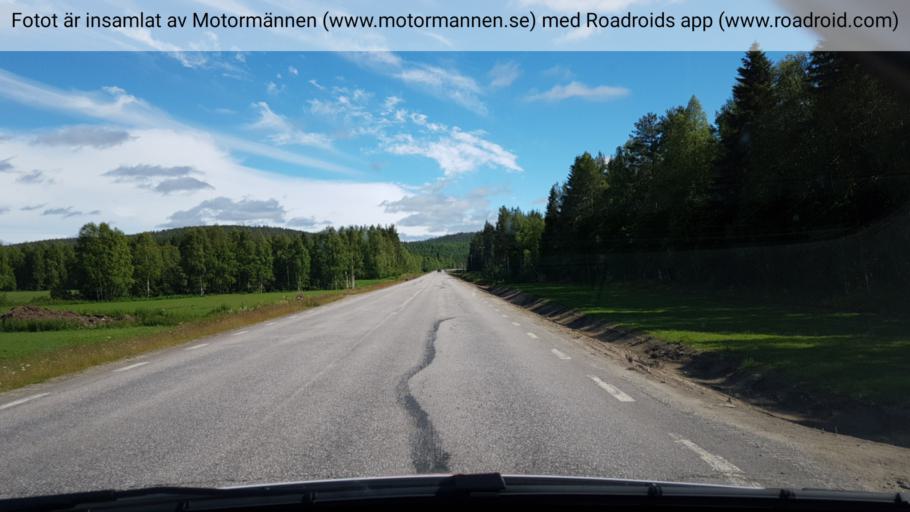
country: SE
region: Vaesterbotten
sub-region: Vindelns Kommun
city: Vindeln
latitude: 64.0496
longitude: 19.6768
